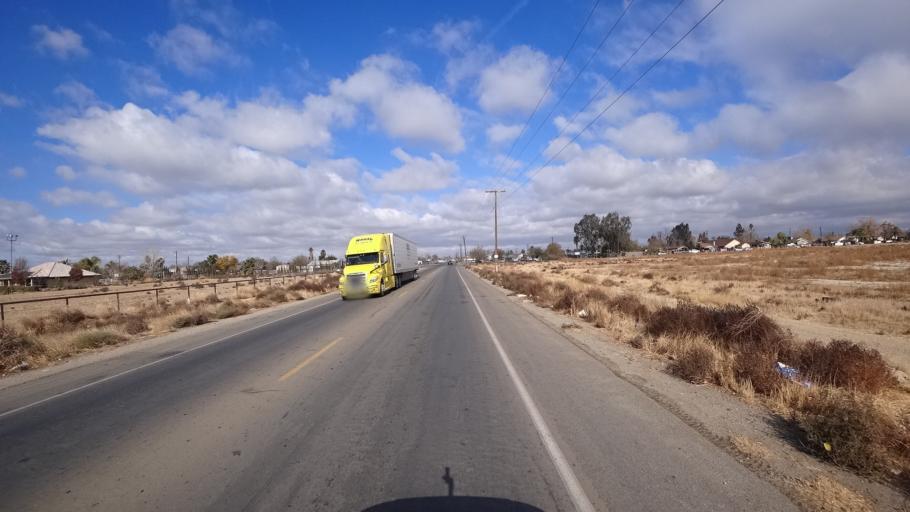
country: US
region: California
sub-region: Kern County
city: Greenfield
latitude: 35.3201
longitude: -118.9854
